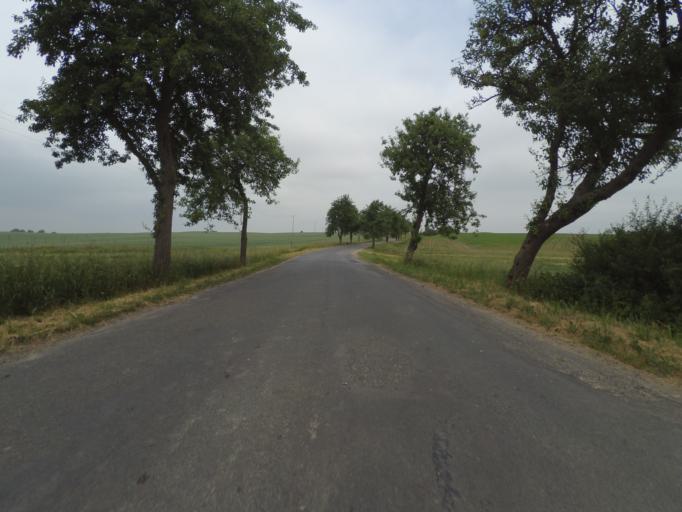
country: DE
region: Mecklenburg-Vorpommern
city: Goldberg
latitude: 53.5147
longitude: 12.1126
